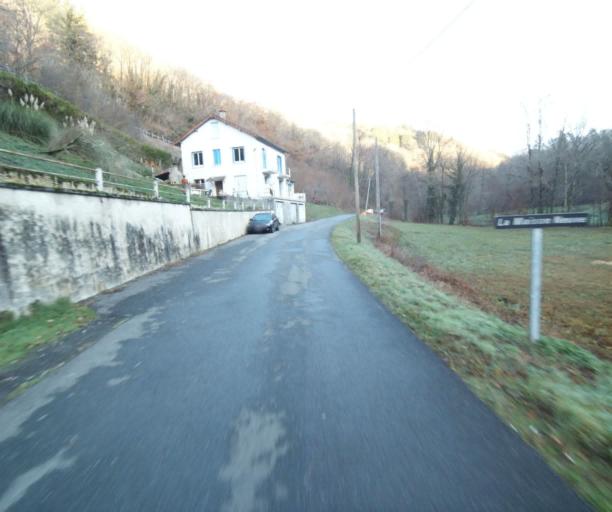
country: FR
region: Limousin
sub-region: Departement de la Correze
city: Laguenne
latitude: 45.2400
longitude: 1.7930
